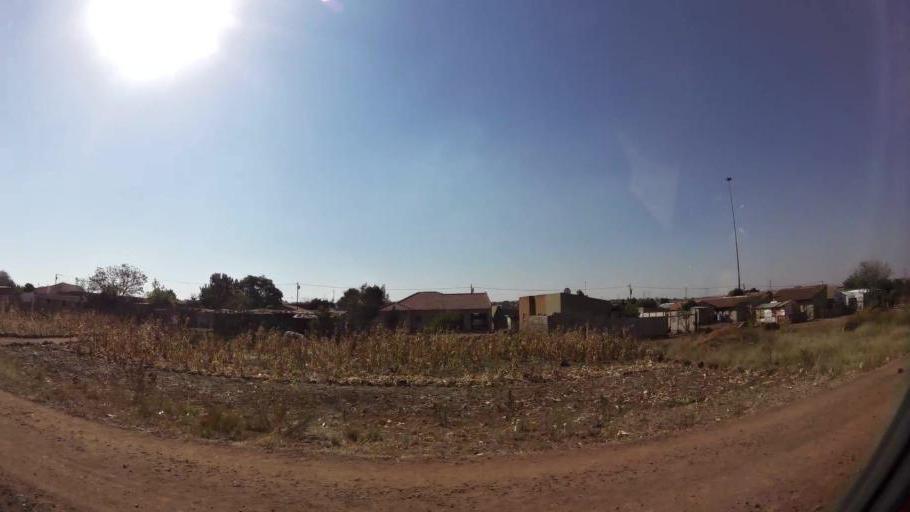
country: ZA
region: Gauteng
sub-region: City of Tshwane Metropolitan Municipality
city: Mabopane
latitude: -25.5549
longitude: 28.0999
